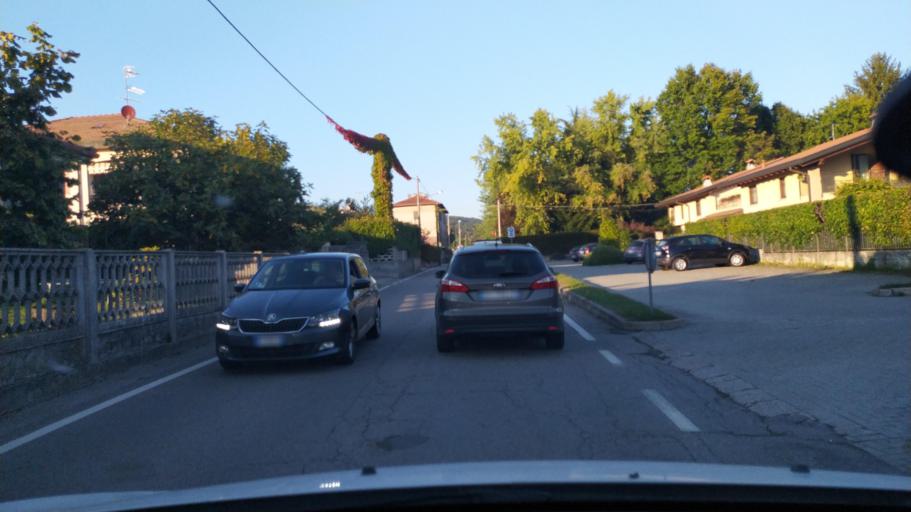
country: IT
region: Lombardy
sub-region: Provincia di Varese
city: Sesto Calende
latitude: 45.7280
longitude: 8.6480
